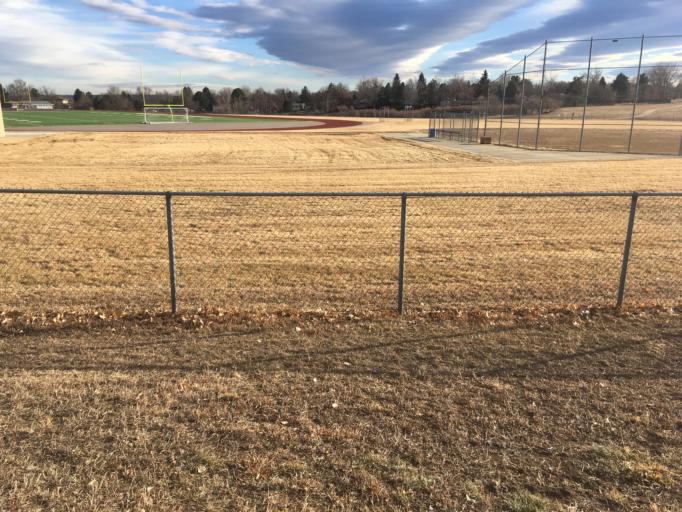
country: US
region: Colorado
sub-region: Broomfield County
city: Broomfield
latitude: 39.9376
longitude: -105.0805
